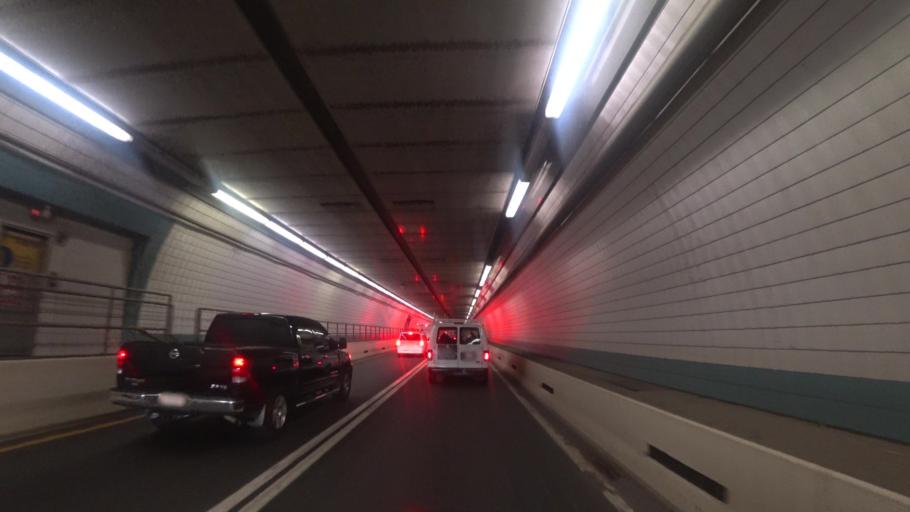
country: US
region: Massachusetts
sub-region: Suffolk County
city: South Boston
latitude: 42.3545
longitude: -71.0328
